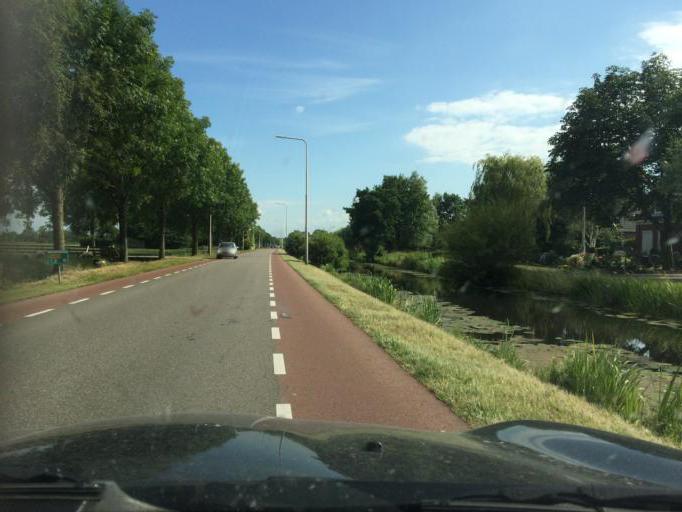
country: NL
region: Utrecht
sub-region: Gemeente Woerden
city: Woerden
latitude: 52.1047
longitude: 4.8944
